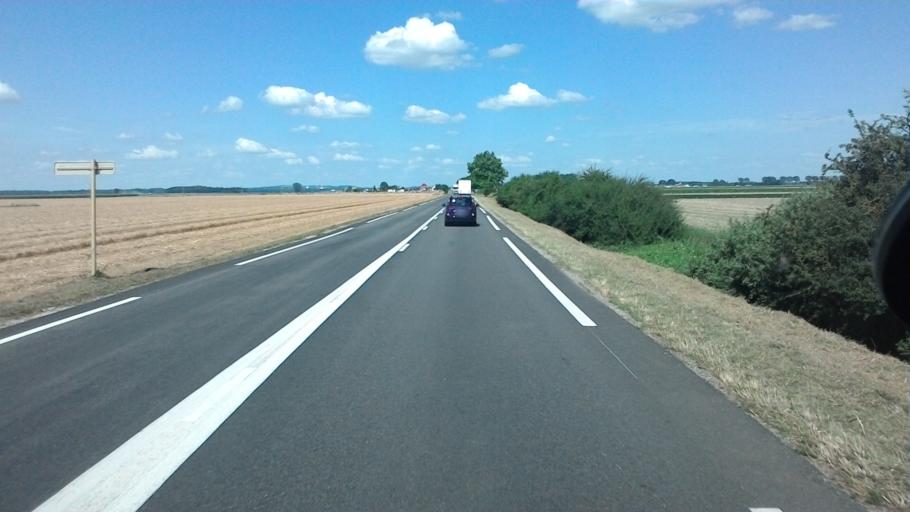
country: FR
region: Franche-Comte
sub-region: Departement du Jura
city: Saint-Aubin
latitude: 46.9970
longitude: 5.3449
